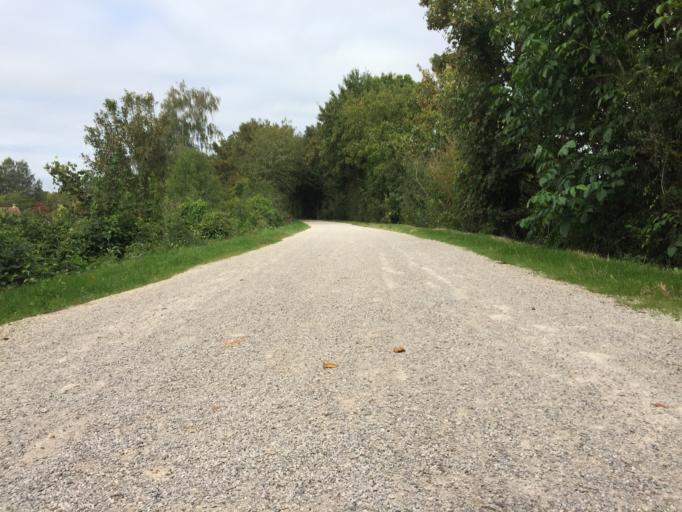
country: FR
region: Picardie
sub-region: Departement de l'Oise
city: Auneuil
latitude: 49.3760
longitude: 1.9931
